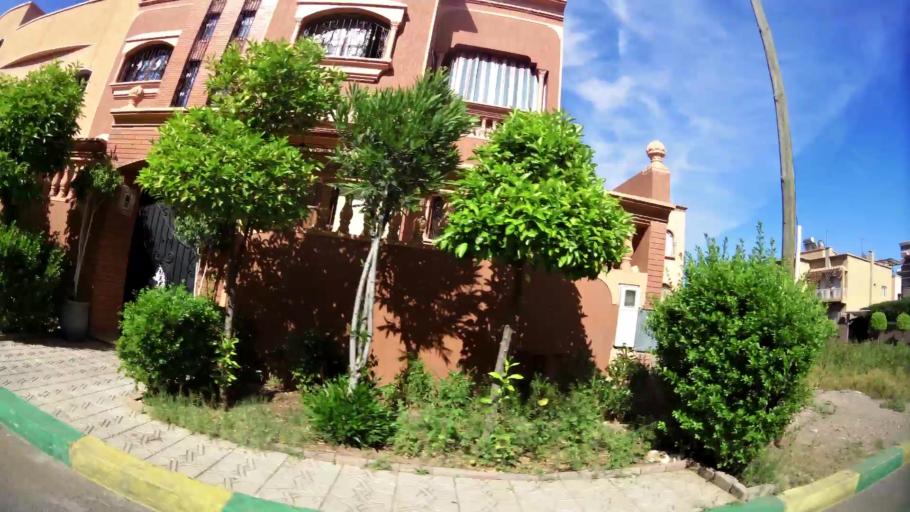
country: MA
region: Marrakech-Tensift-Al Haouz
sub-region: Marrakech
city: Marrakesh
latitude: 31.6488
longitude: -8.0486
